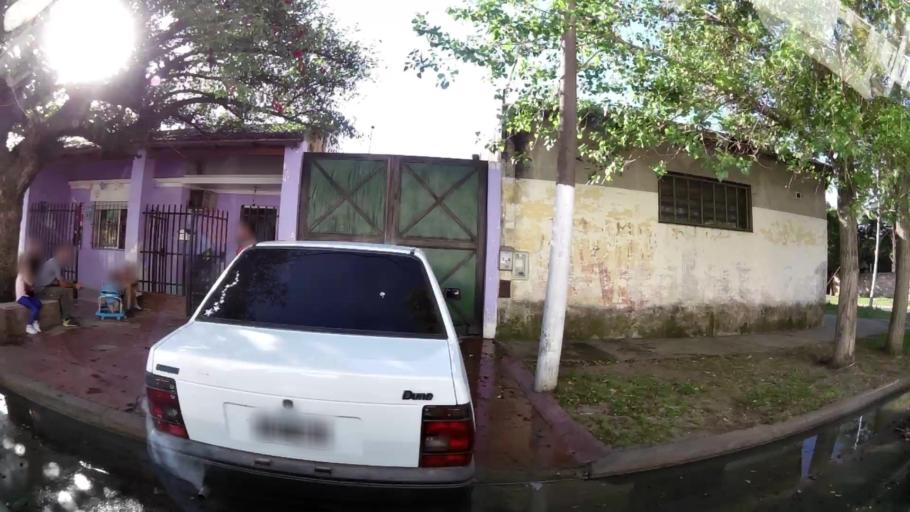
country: AR
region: Buenos Aires
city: Hurlingham
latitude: -34.5681
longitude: -58.6103
